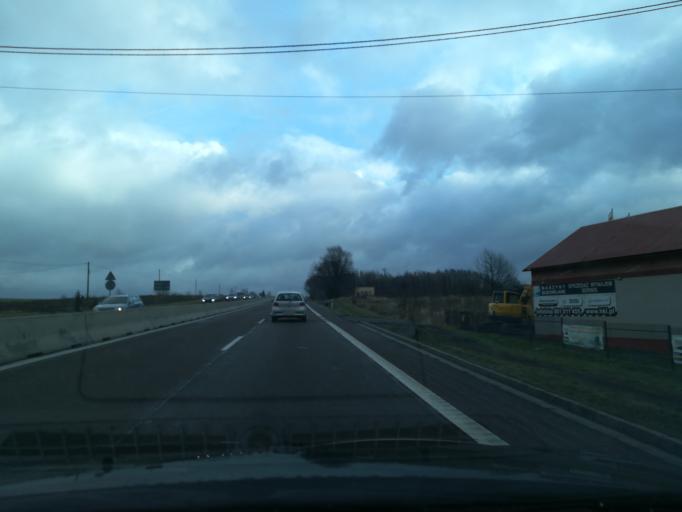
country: PL
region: Subcarpathian Voivodeship
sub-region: Powiat lancucki
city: Kraczkowa
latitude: 50.0474
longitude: 22.1661
